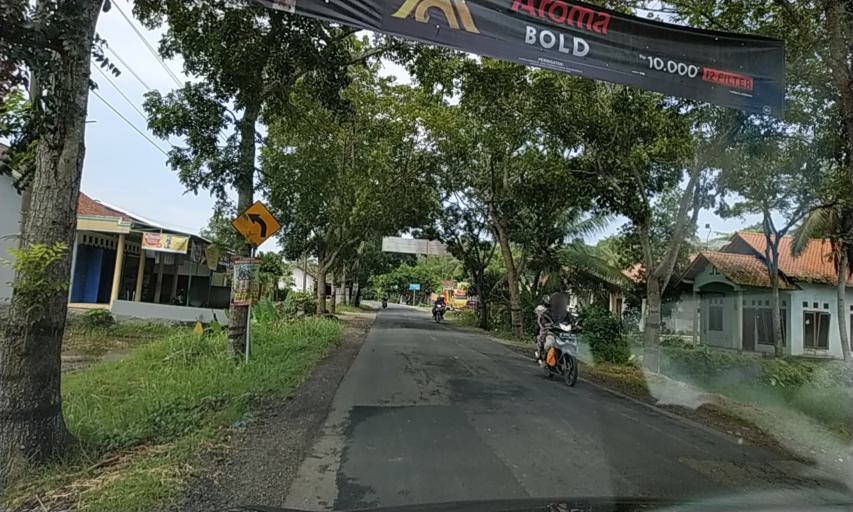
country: ID
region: Central Java
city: Mulyosari
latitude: -7.5205
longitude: 108.7842
